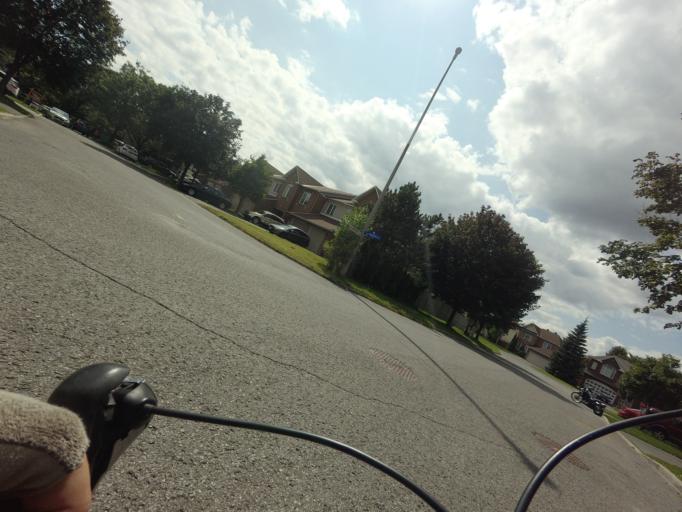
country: CA
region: Ontario
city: Bells Corners
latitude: 45.2791
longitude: -75.8458
